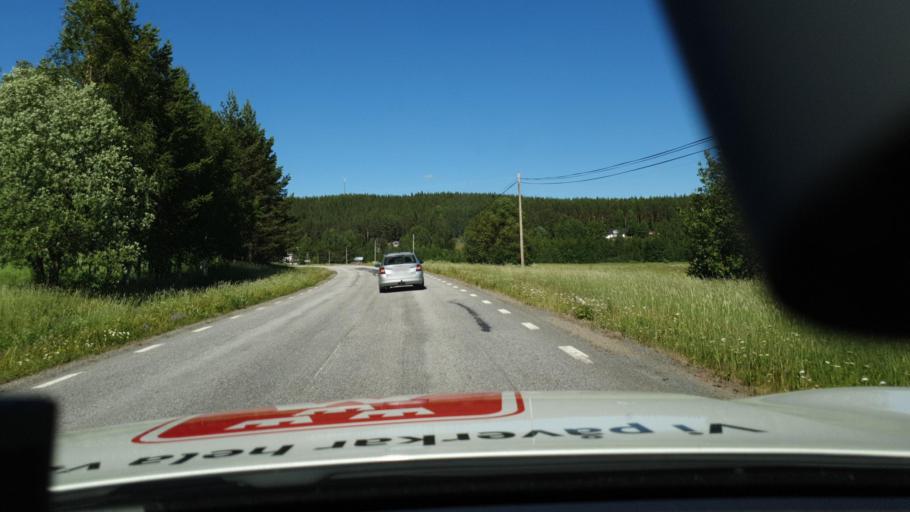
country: SE
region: Norrbotten
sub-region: Bodens Kommun
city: Saevast
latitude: 65.8698
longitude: 21.8756
